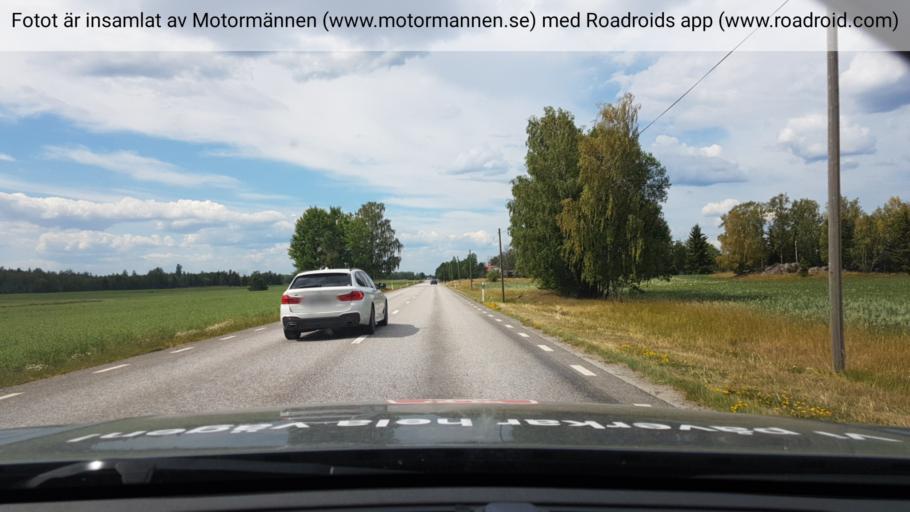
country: SE
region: Vaestmanland
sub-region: Sala Kommun
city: Sala
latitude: 59.8394
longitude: 16.6801
